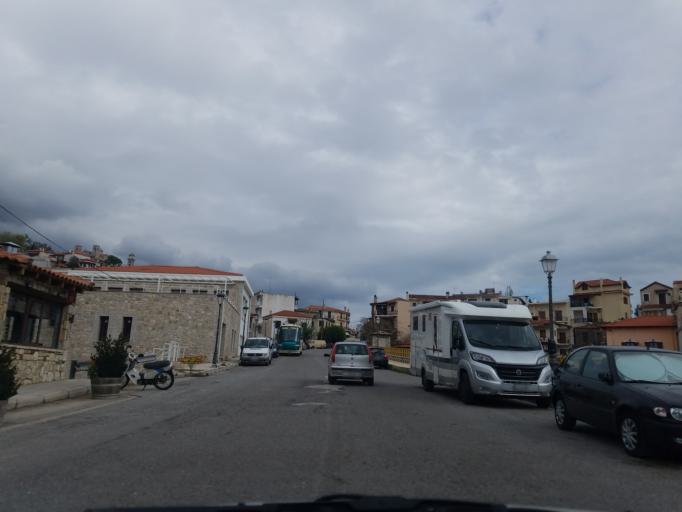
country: GR
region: Central Greece
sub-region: Nomos Voiotias
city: Arachova
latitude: 38.4793
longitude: 22.5798
